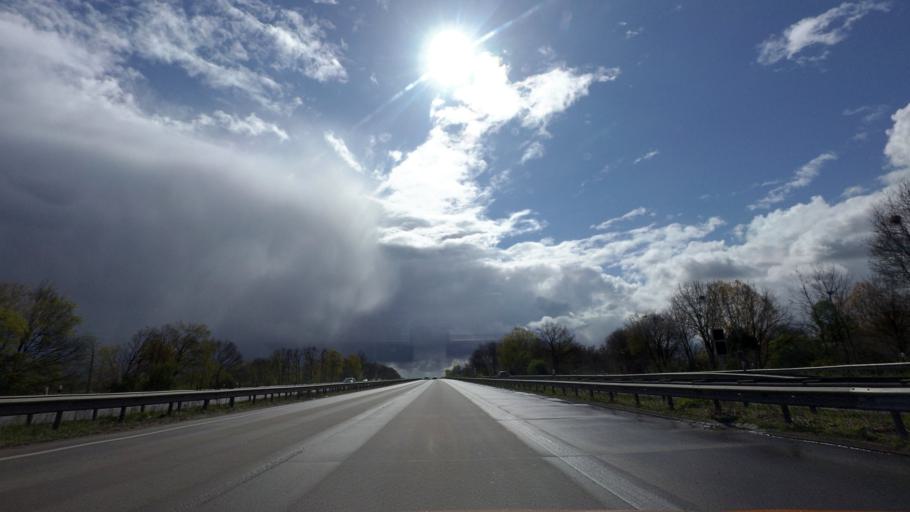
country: DE
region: Lower Saxony
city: Oyten
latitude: 53.0442
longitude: 8.9795
